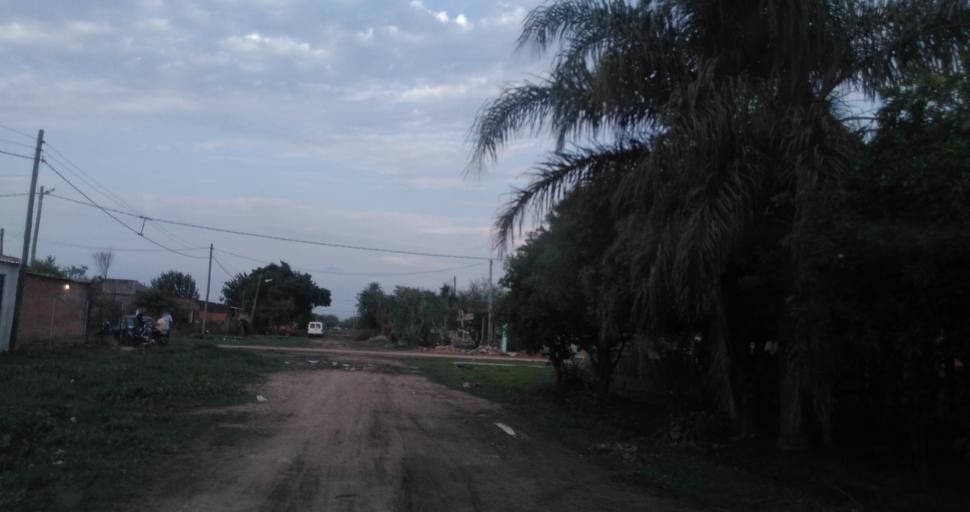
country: AR
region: Chaco
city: Resistencia
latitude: -27.4835
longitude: -59.0049
